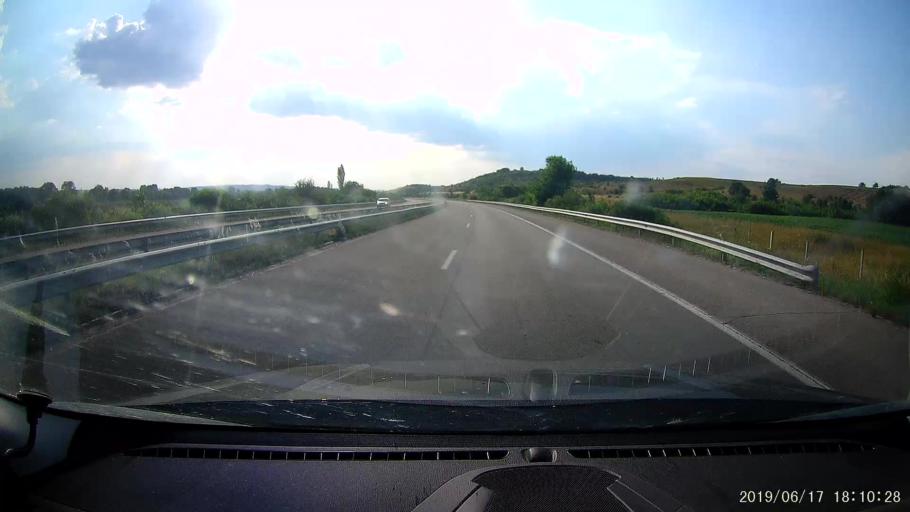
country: BG
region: Khaskovo
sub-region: Obshtina Lyubimets
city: Lyubimets
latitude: 41.8749
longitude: 26.0767
